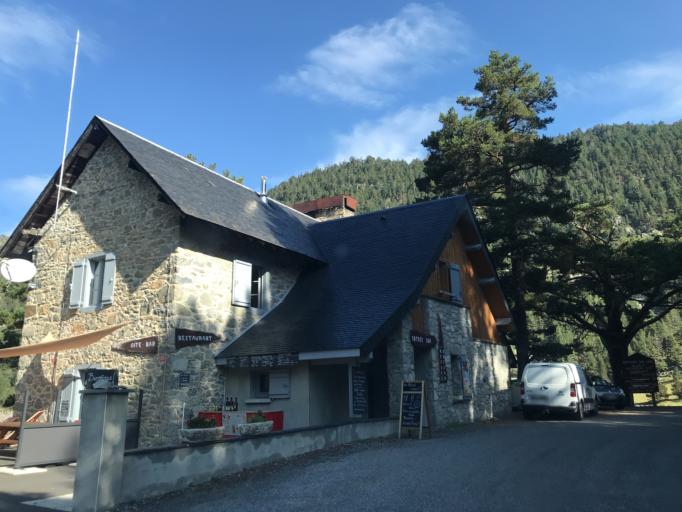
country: FR
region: Midi-Pyrenees
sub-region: Departement des Hautes-Pyrenees
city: Saint-Lary-Soulan
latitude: 42.8262
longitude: 0.1684
